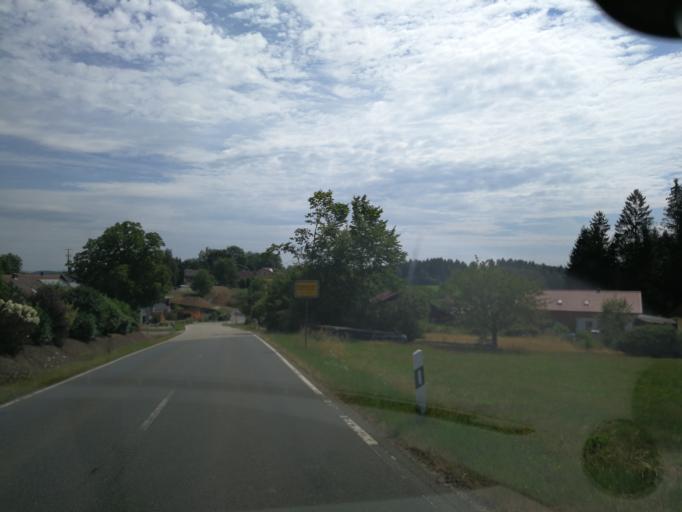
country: DE
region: Bavaria
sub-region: Upper Palatinate
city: Falkenstein
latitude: 49.0900
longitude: 12.4969
